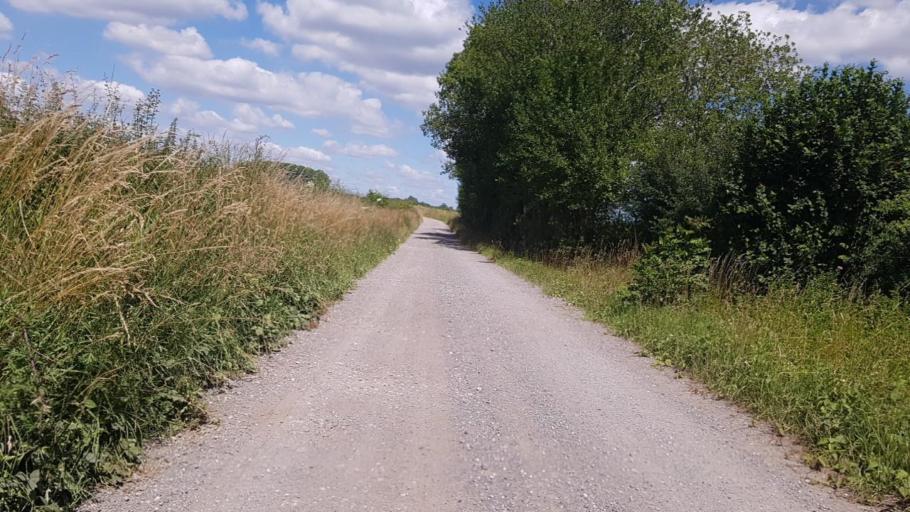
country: BE
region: Wallonia
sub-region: Province du Hainaut
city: Thuin
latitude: 50.3166
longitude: 4.3541
